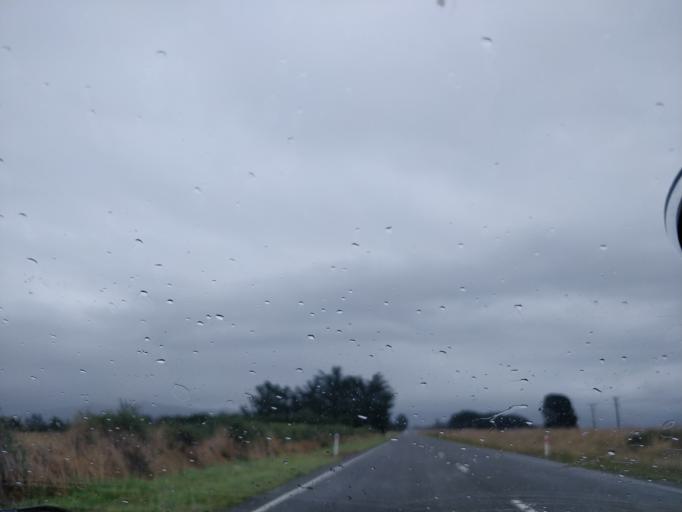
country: NZ
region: Canterbury
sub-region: Selwyn District
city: Darfield
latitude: -43.3831
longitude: 172.0093
